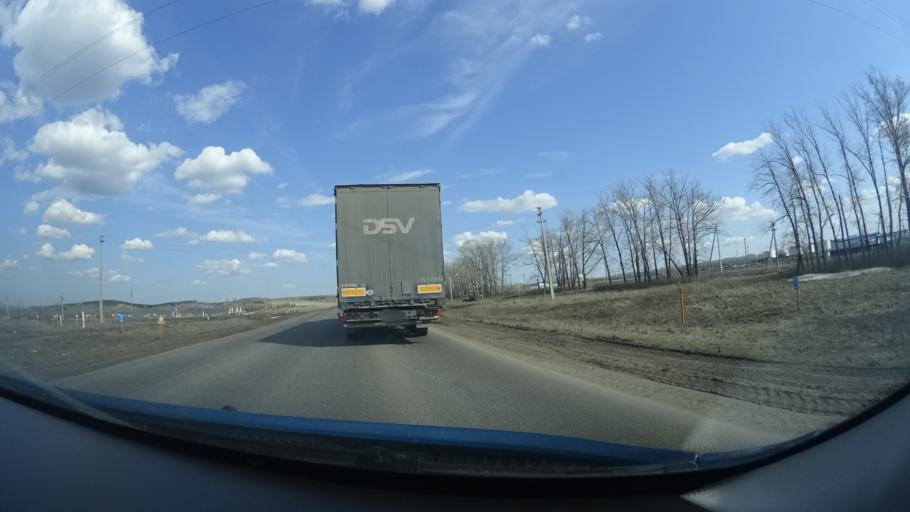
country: RU
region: Bashkortostan
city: Buzdyak
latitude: 54.6752
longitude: 54.7820
